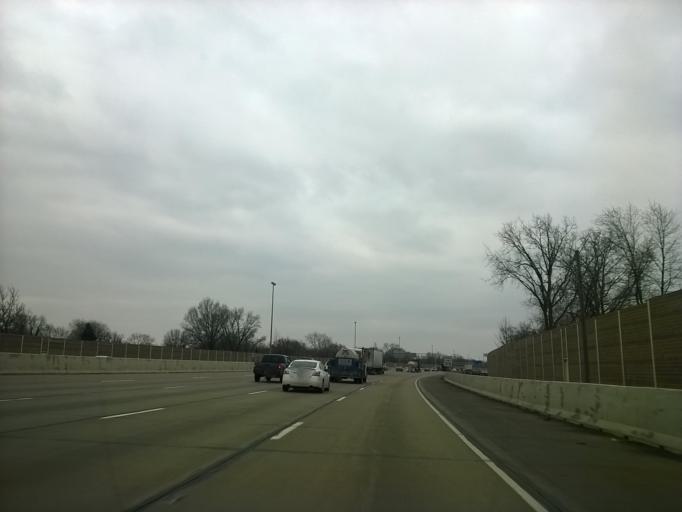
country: US
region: Indiana
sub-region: Marion County
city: Lawrence
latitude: 39.8245
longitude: -86.0318
